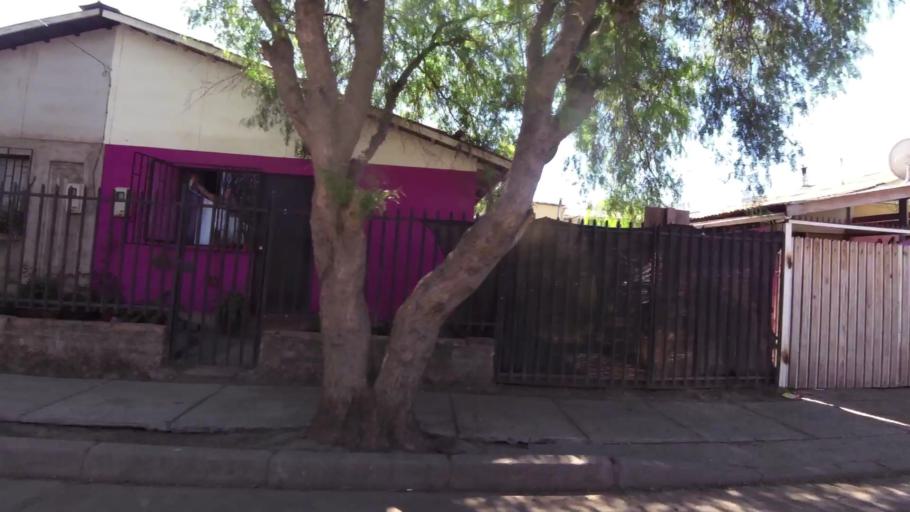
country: CL
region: O'Higgins
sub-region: Provincia de Colchagua
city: Chimbarongo
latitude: -34.5726
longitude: -71.0021
